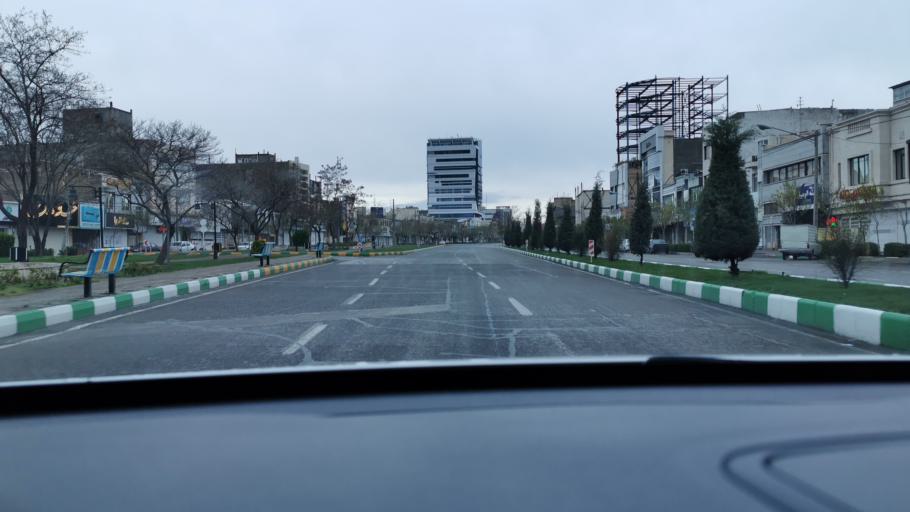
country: IR
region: Razavi Khorasan
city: Mashhad
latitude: 36.3291
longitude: 59.5270
